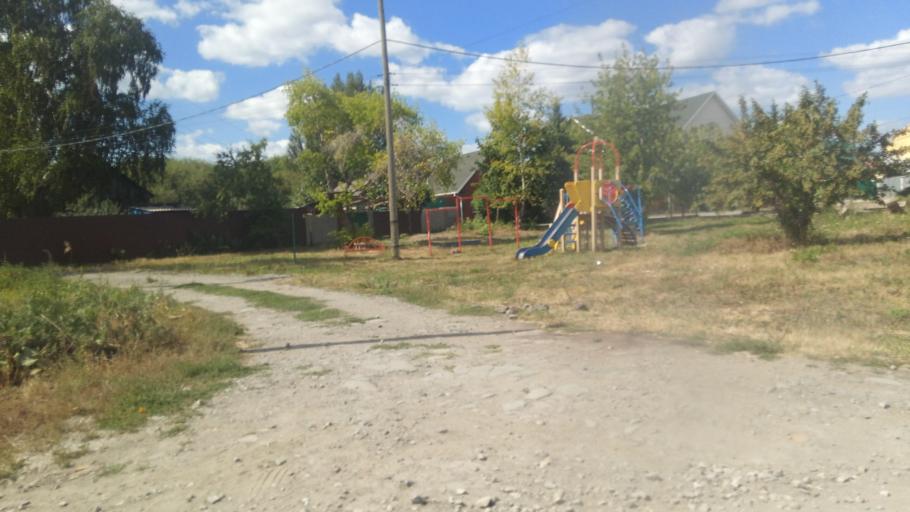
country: RU
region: Chelyabinsk
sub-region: Gorod Chelyabinsk
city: Chelyabinsk
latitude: 55.1263
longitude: 61.3913
